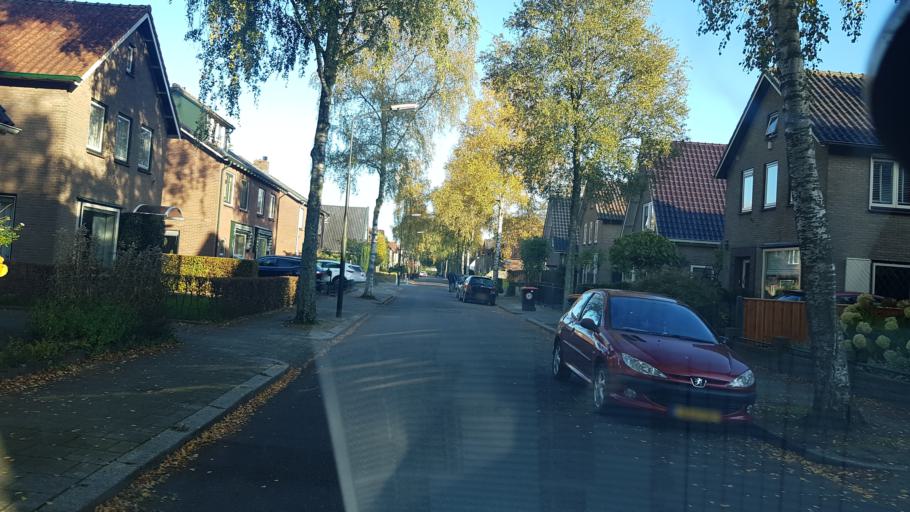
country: NL
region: Gelderland
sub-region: Gemeente Apeldoorn
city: Apeldoorn
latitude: 52.1866
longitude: 5.9664
